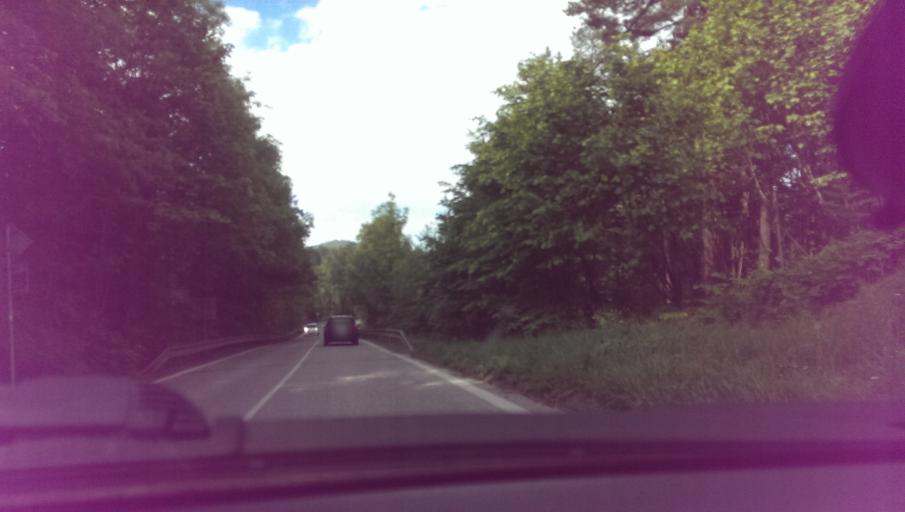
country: CZ
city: Trojanovice
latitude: 49.5187
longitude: 18.2171
